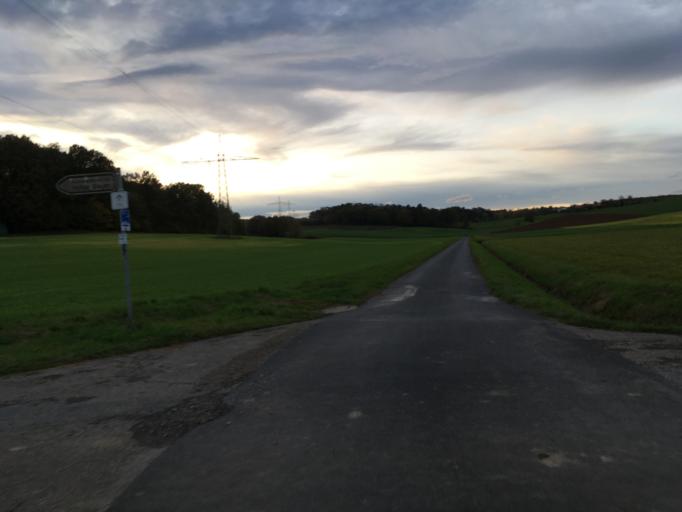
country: DE
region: Baden-Wuerttemberg
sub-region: Karlsruhe Region
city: Rosenberg
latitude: 49.3914
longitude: 9.4927
